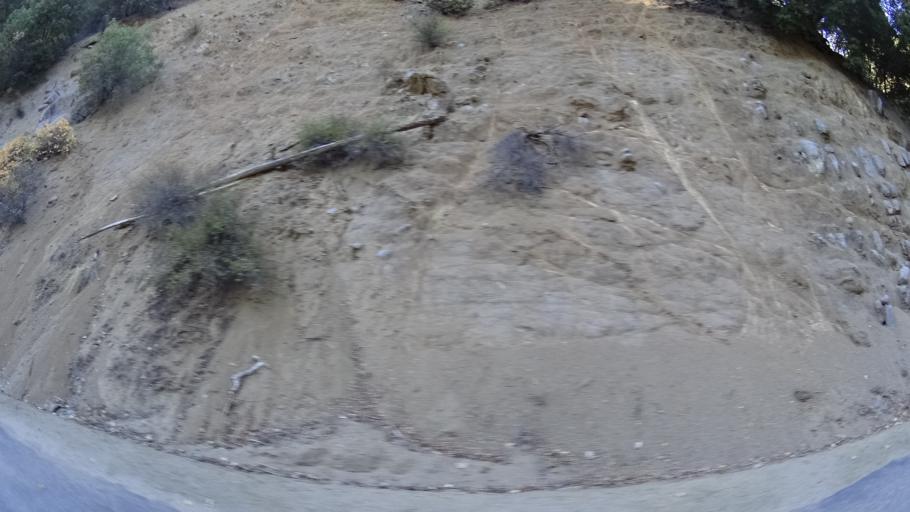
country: US
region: California
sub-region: Humboldt County
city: Willow Creek
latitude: 41.2854
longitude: -123.2552
